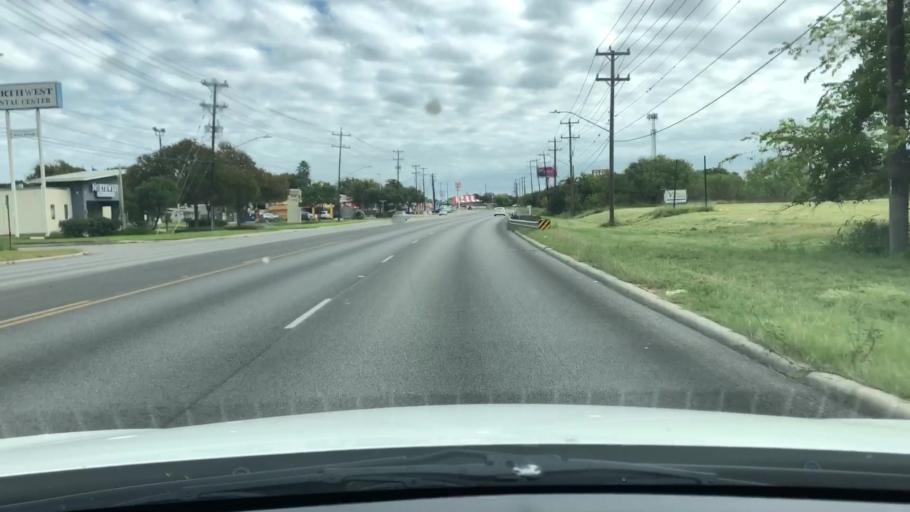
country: US
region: Texas
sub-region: Bexar County
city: Leon Valley
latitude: 29.4825
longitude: -98.6623
